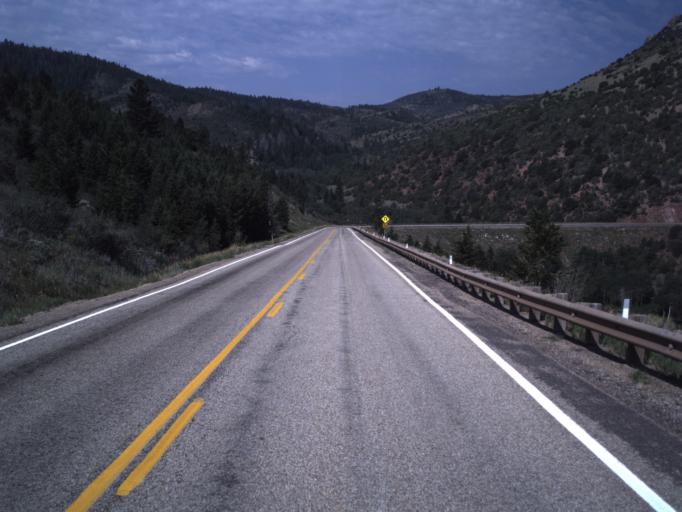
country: US
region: Utah
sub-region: Daggett County
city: Manila
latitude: 40.8916
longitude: -109.7160
